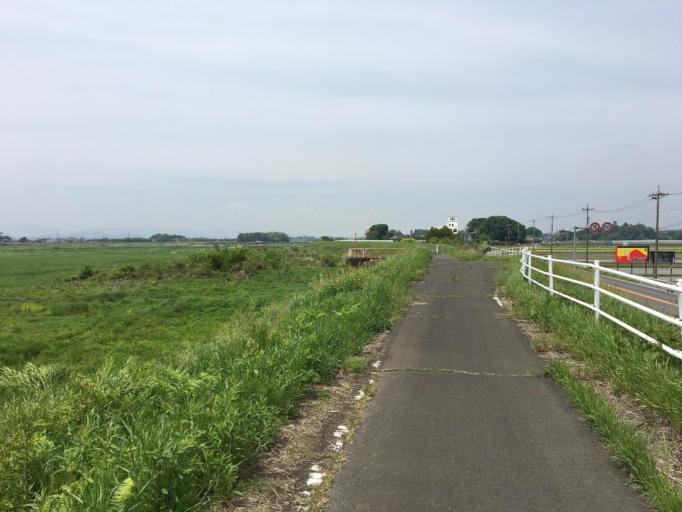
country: JP
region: Tochigi
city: Mibu
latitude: 36.3614
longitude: 139.8065
